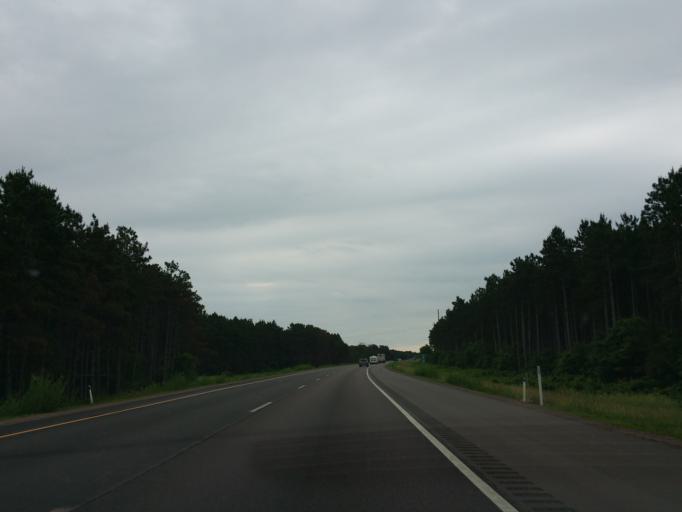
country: US
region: Wisconsin
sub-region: Trempealeau County
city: Osseo
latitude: 44.5631
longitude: -91.1852
